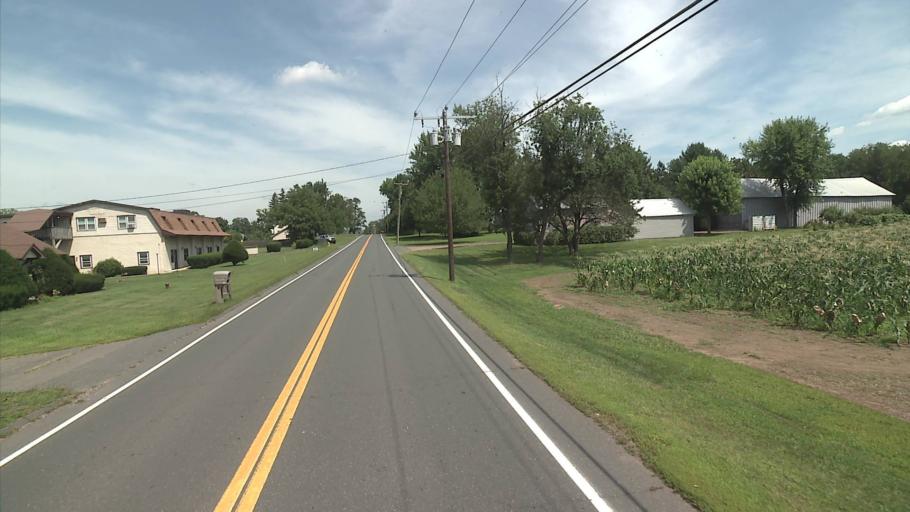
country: US
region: Connecticut
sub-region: Tolland County
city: Ellington
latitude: 41.8985
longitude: -72.4790
